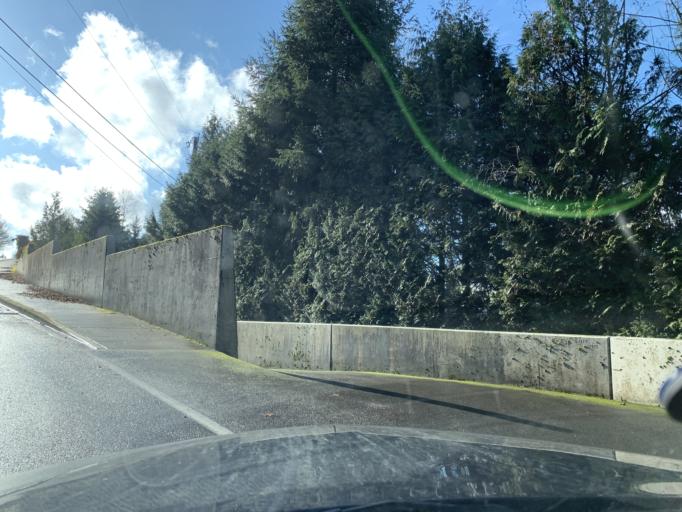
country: US
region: Washington
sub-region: King County
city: Mercer Island
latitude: 47.5927
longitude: -122.2466
